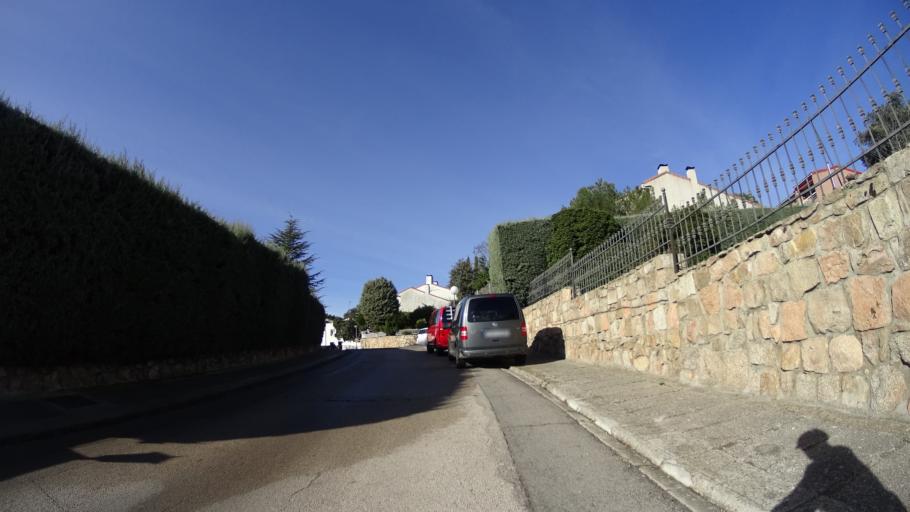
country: ES
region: Madrid
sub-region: Provincia de Madrid
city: Torrelodones
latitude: 40.6069
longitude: -3.9418
